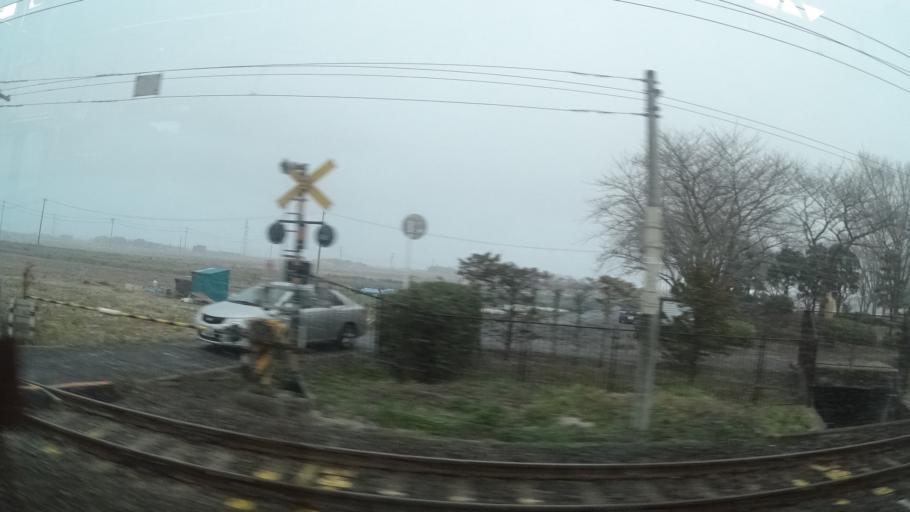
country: JP
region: Miyagi
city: Watari
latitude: 38.0420
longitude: 140.8598
